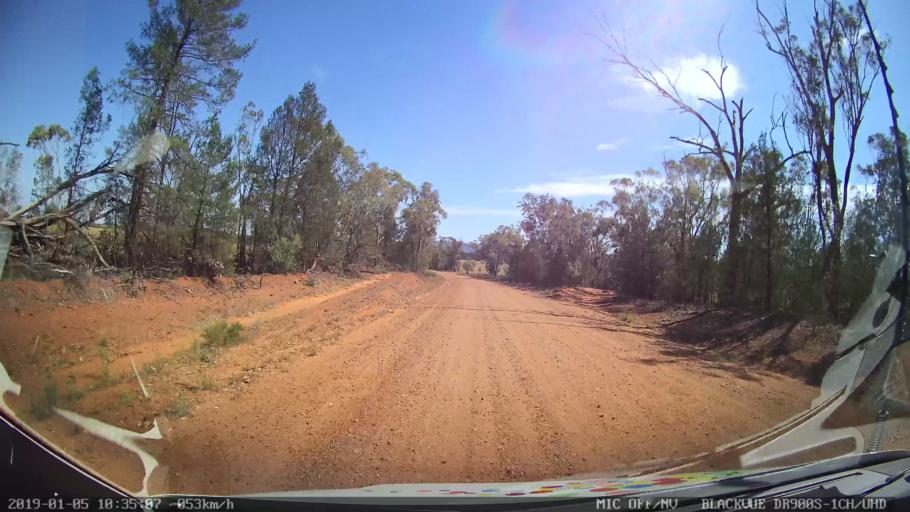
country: AU
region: New South Wales
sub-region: Gilgandra
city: Gilgandra
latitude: -31.4930
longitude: 148.9295
